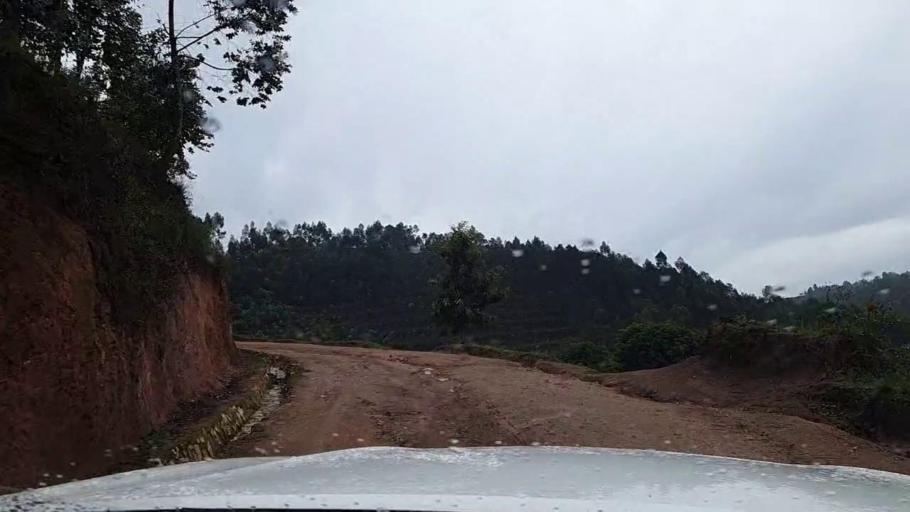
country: RW
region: Southern Province
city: Nzega
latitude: -2.4678
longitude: 29.5042
